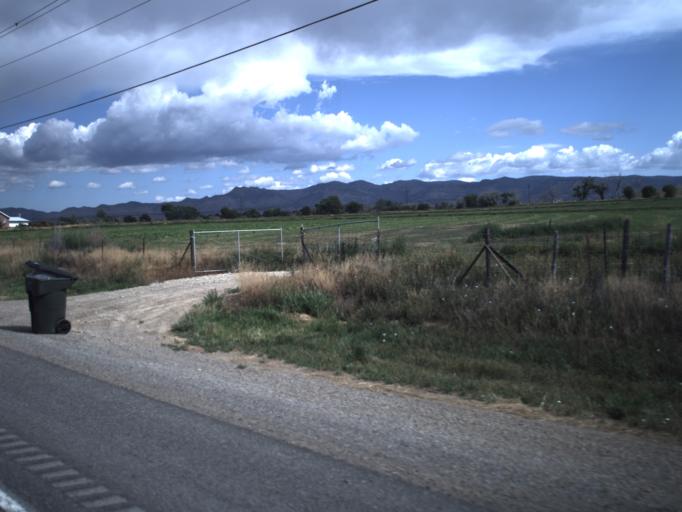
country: US
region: Utah
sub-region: Carbon County
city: Wellington
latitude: 39.5572
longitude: -110.7621
